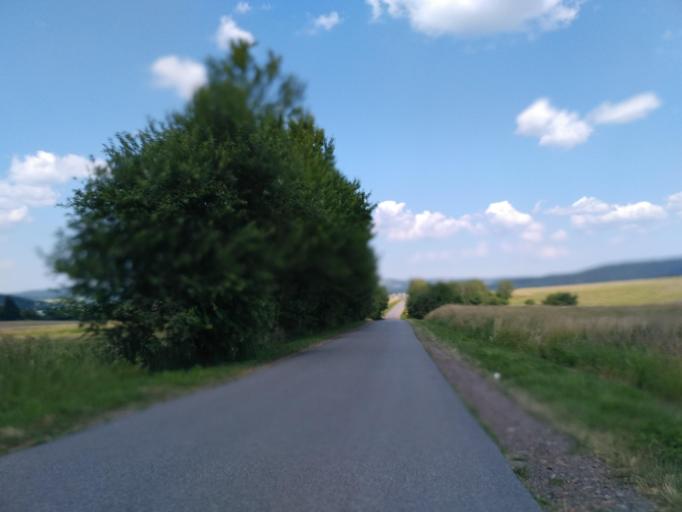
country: PL
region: Subcarpathian Voivodeship
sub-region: Powiat sanocki
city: Strachocina
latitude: 49.5844
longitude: 22.1277
